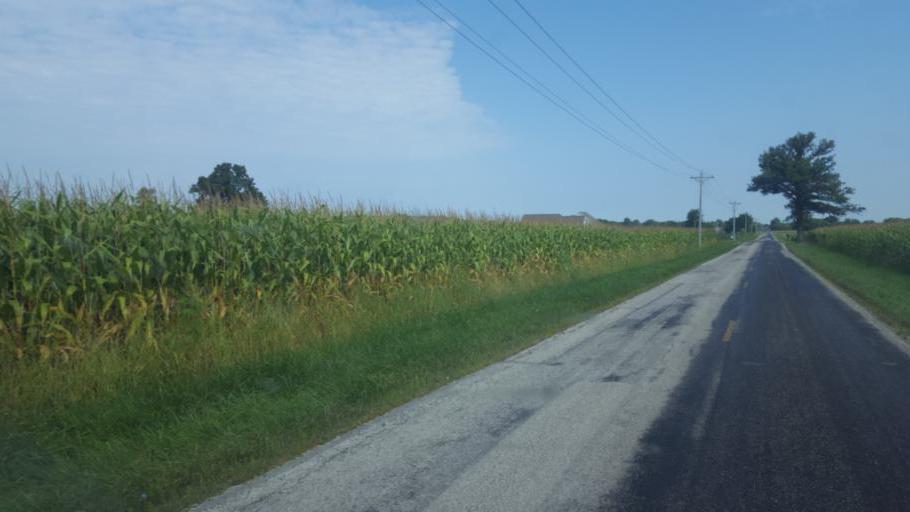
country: US
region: Ohio
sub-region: Morrow County
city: Cardington
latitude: 40.5153
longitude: -82.9955
